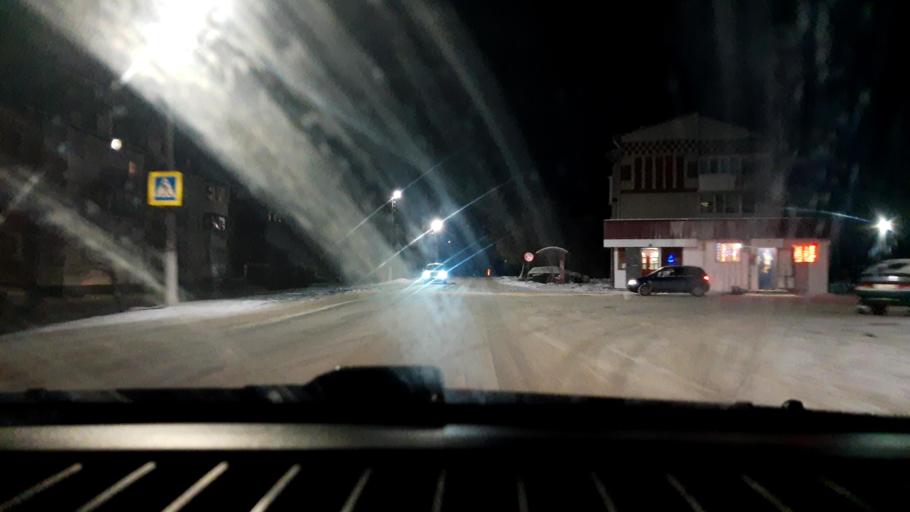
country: RU
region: Nizjnij Novgorod
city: Bogorodsk
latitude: 56.0954
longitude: 43.5380
